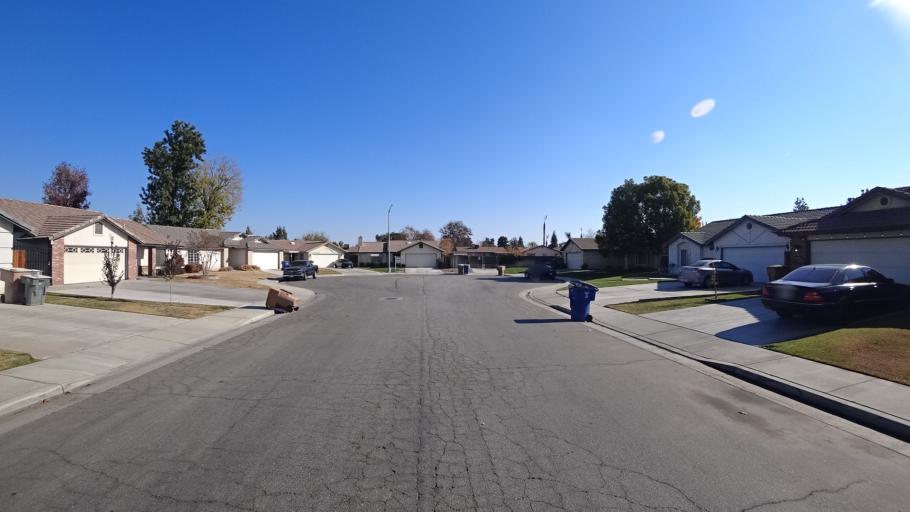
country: US
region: California
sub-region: Kern County
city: Greenfield
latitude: 35.3007
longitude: -119.0557
